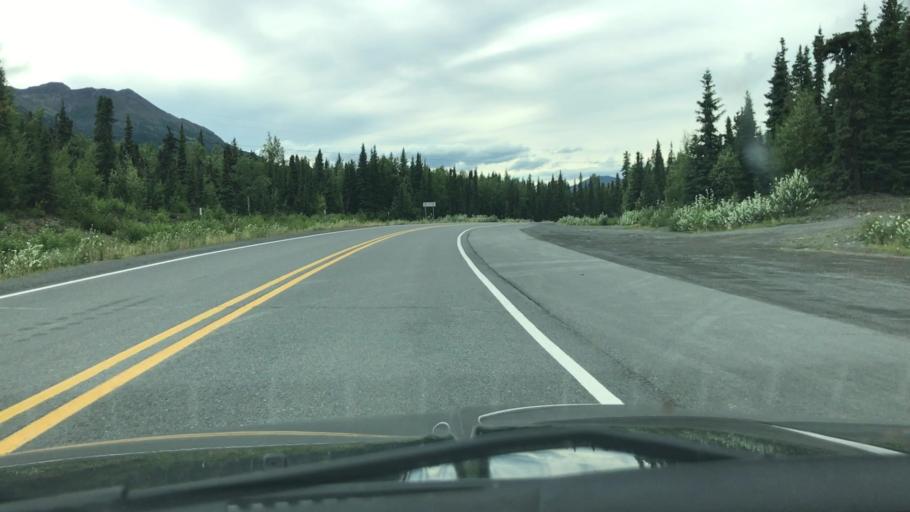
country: US
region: Alaska
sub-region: Kenai Peninsula Borough
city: Seward
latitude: 60.4836
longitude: -149.9534
